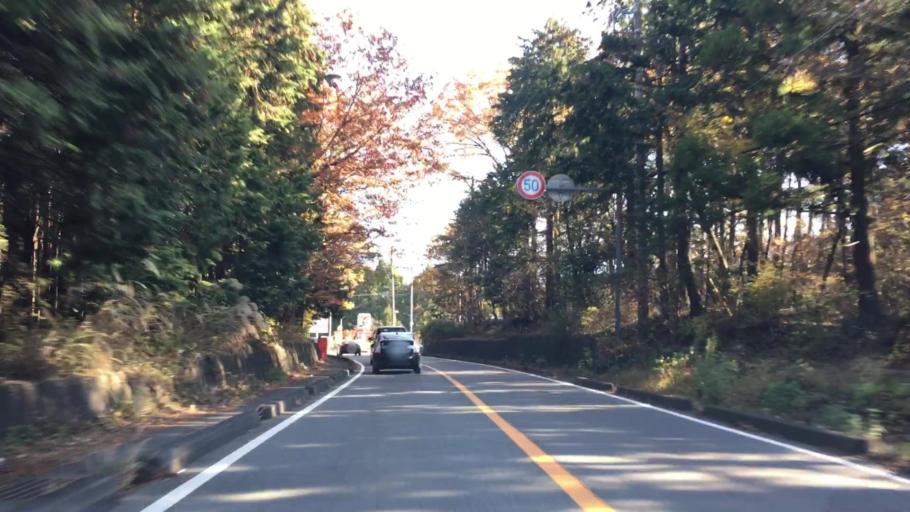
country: JP
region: Shizuoka
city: Gotemba
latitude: 35.3323
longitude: 138.9010
